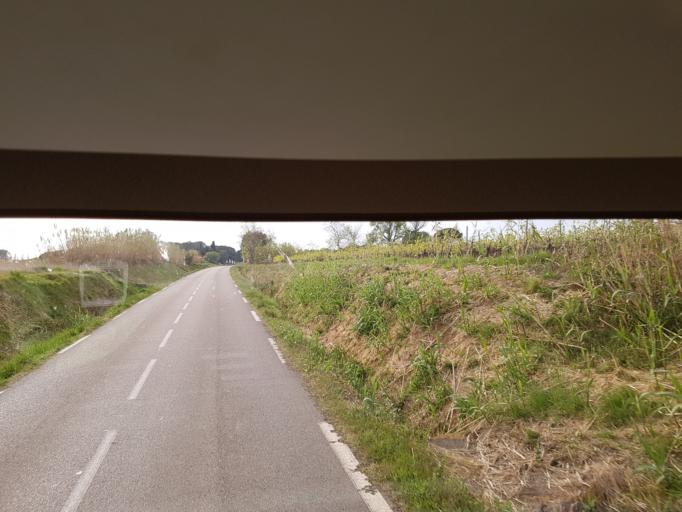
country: FR
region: Languedoc-Roussillon
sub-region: Departement de l'Herault
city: Pomerols
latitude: 43.3683
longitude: 3.5057
